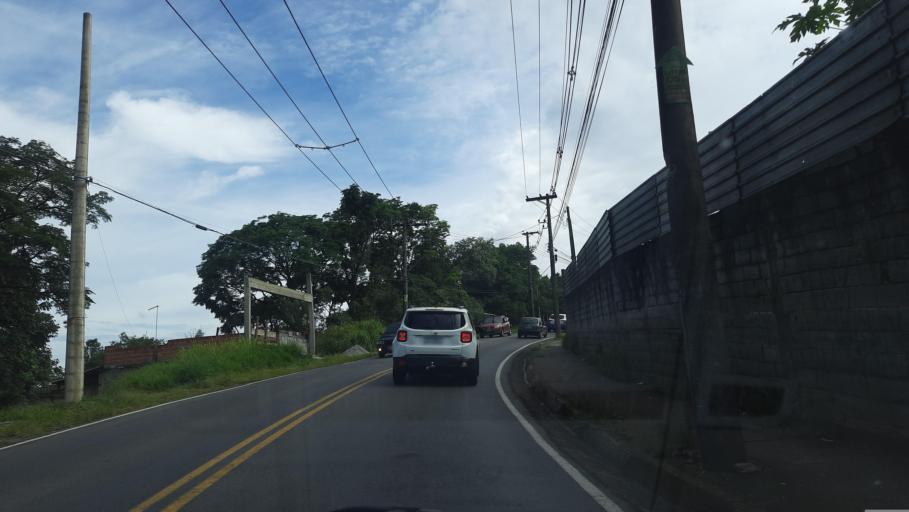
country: BR
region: Sao Paulo
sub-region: Caieiras
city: Caieiras
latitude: -23.3864
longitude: -46.7124
